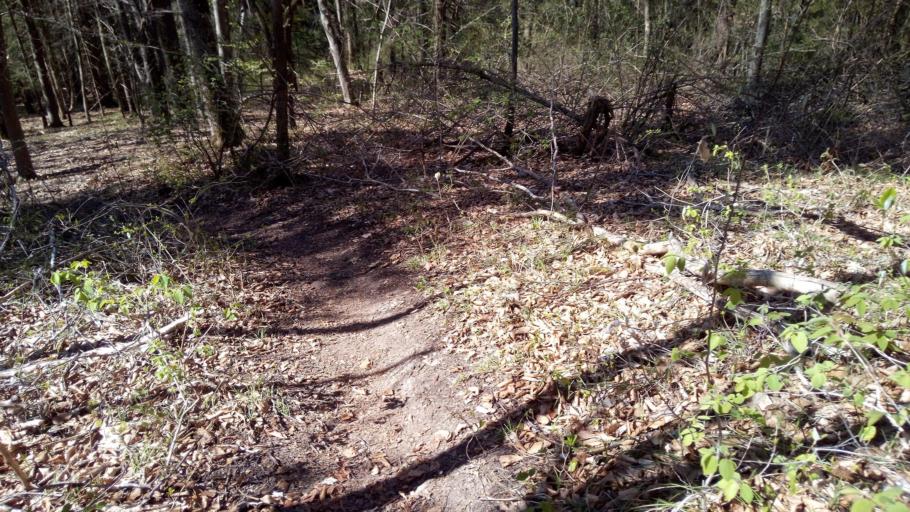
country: DE
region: Baden-Wuerttemberg
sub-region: Regierungsbezirk Stuttgart
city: Donzdorf
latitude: 48.7102
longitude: 9.8440
